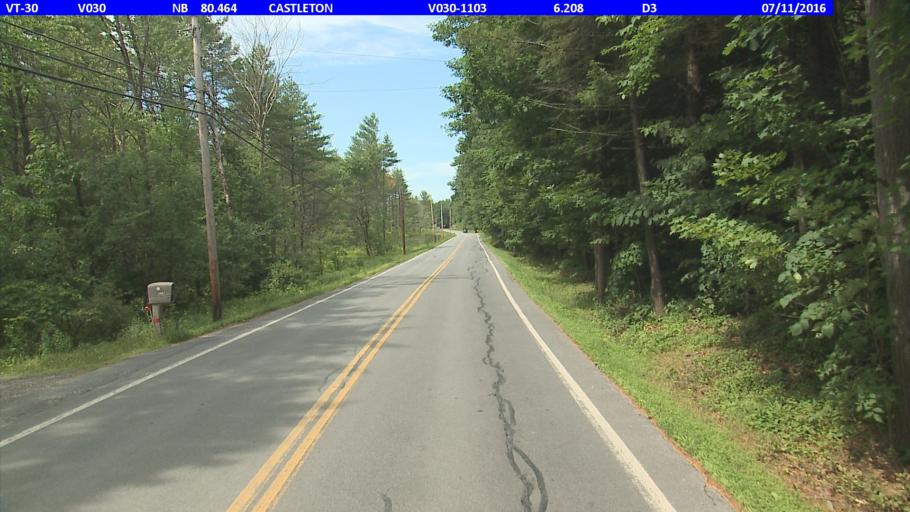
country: US
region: Vermont
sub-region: Rutland County
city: Castleton
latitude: 43.6741
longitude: -73.1916
